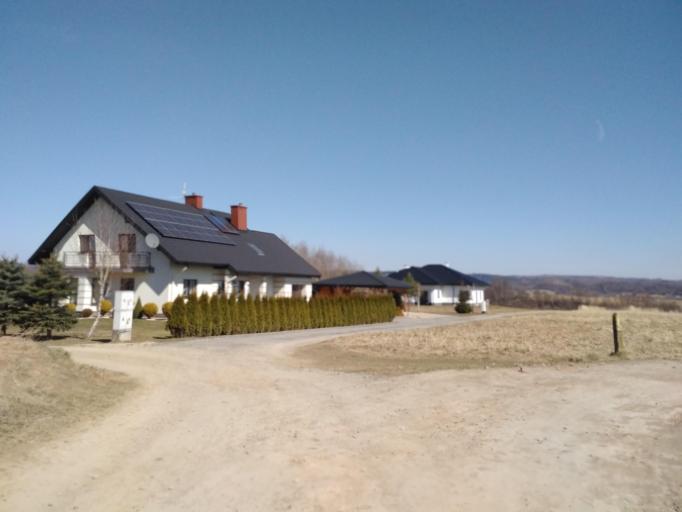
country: PL
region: Subcarpathian Voivodeship
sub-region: Powiat brzozowski
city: Orzechowka
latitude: 49.7207
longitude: 21.9680
